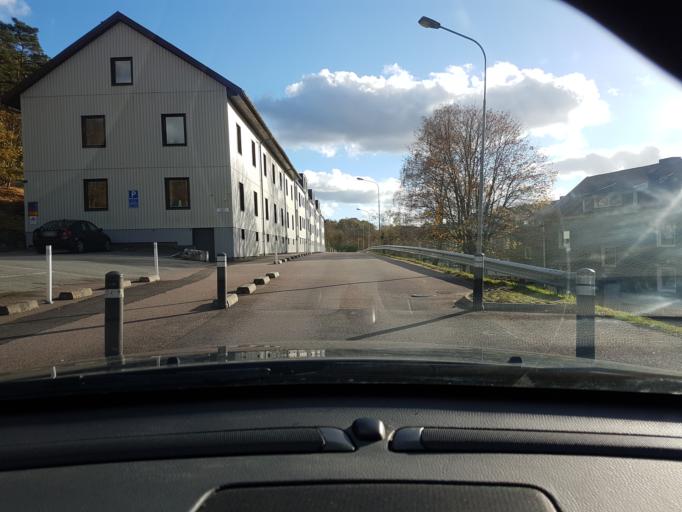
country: SE
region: Vaestra Goetaland
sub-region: Ale Kommun
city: Surte
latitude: 57.8323
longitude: 12.0212
